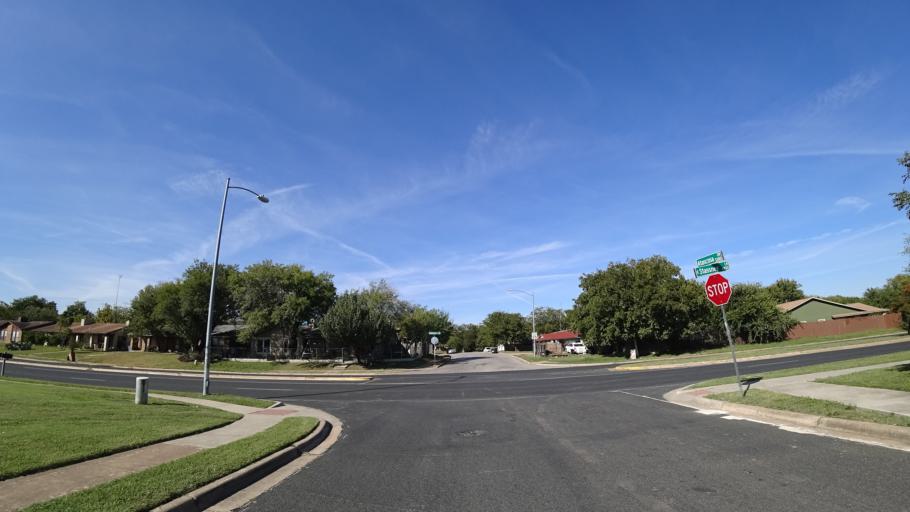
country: US
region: Texas
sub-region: Travis County
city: Onion Creek
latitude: 30.1938
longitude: -97.7411
